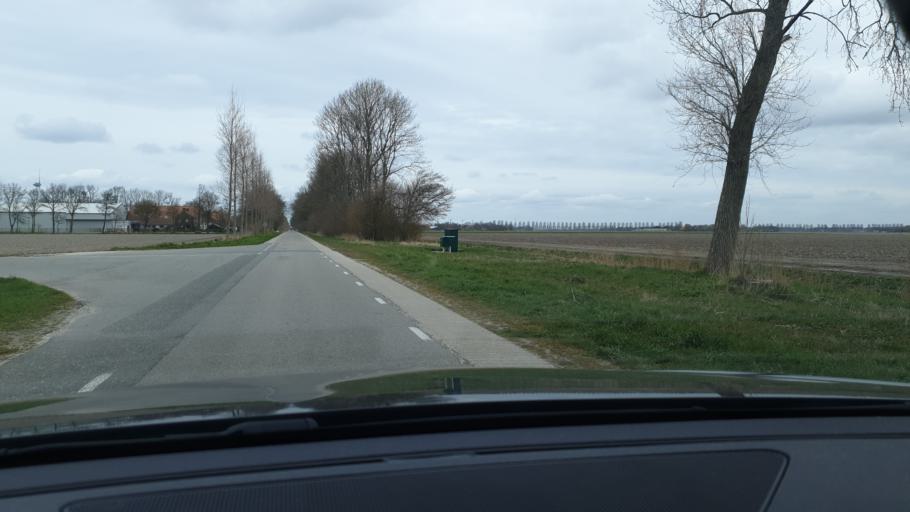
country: NL
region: Flevoland
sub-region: Gemeente Urk
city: Urk
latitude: 52.7259
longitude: 5.6078
